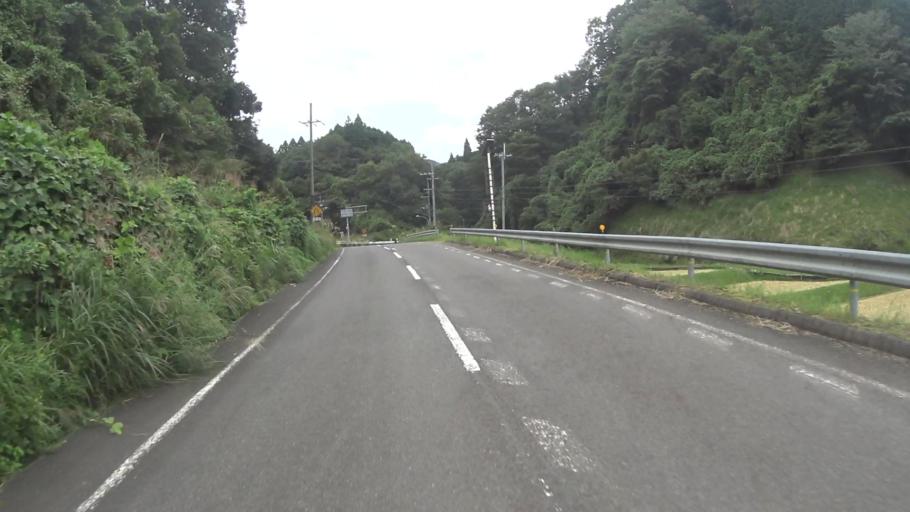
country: JP
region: Kyoto
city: Uji
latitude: 34.8554
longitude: 135.9392
